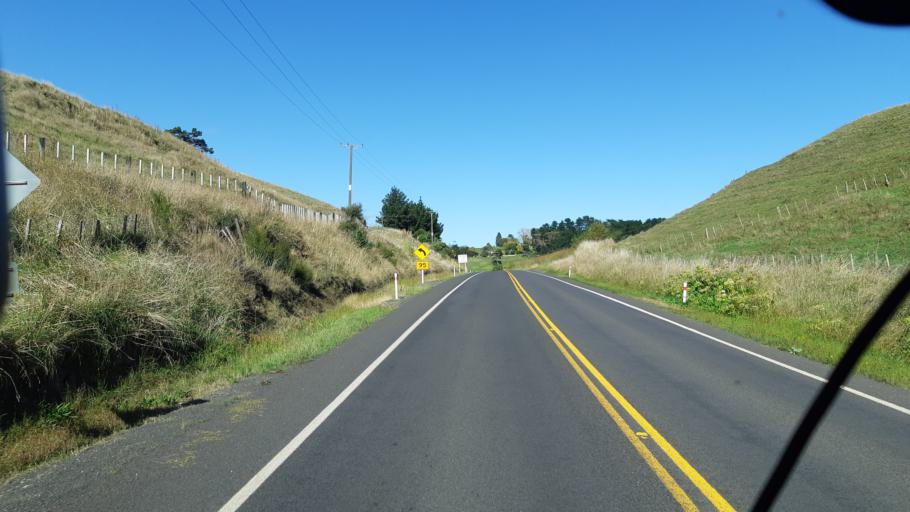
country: NZ
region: Manawatu-Wanganui
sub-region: Wanganui District
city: Wanganui
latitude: -39.9629
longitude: 175.1003
